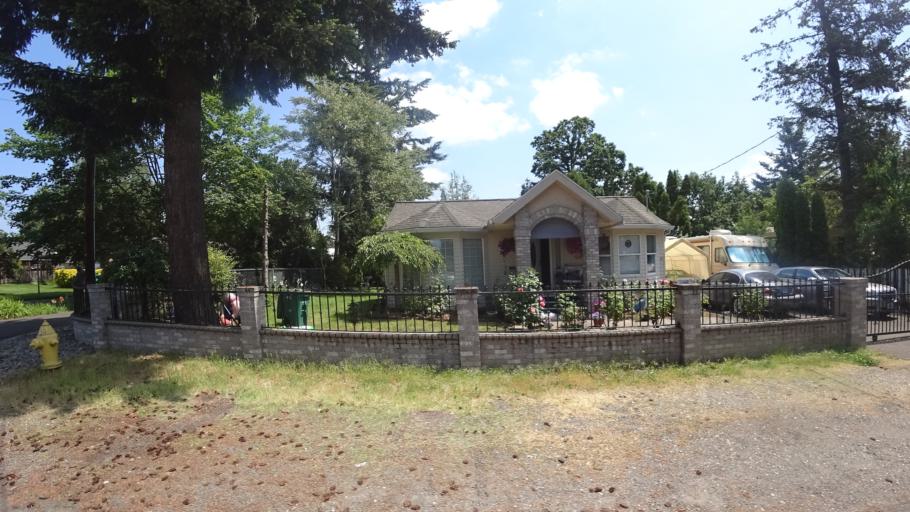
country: US
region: Oregon
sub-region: Multnomah County
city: Fairview
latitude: 45.5280
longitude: -122.5014
